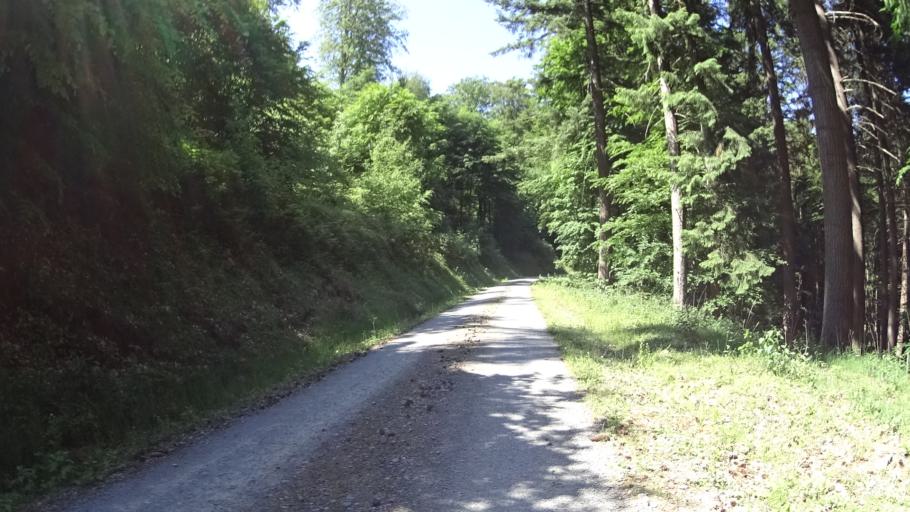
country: DE
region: Baden-Wuerttemberg
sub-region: Karlsruhe Region
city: Wilhelmsfeld
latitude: 49.4378
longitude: 8.7710
